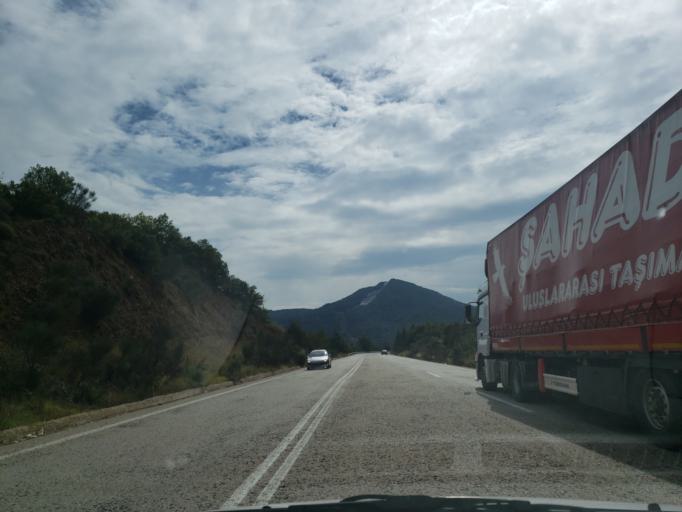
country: GR
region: Central Greece
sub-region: Nomos Fthiotidos
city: Stavros
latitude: 39.0214
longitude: 22.3746
